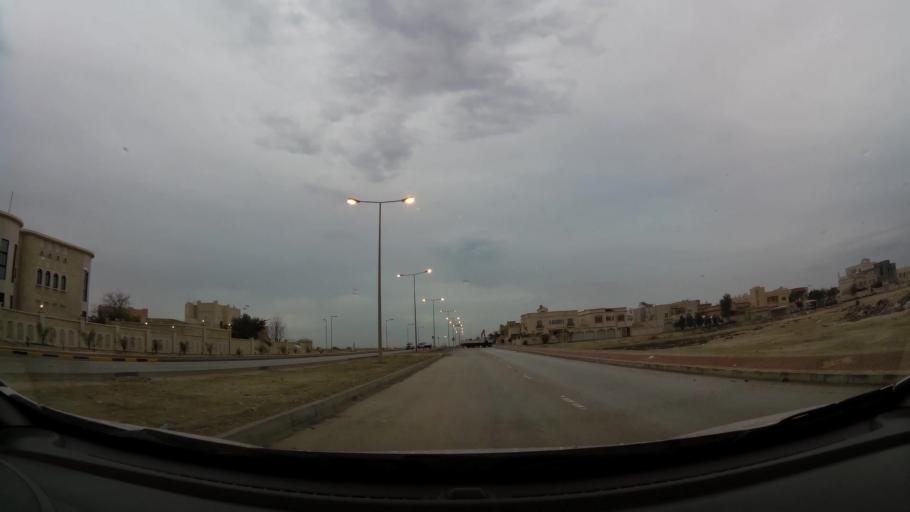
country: BH
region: Central Governorate
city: Madinat Hamad
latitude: 26.1447
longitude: 50.5171
